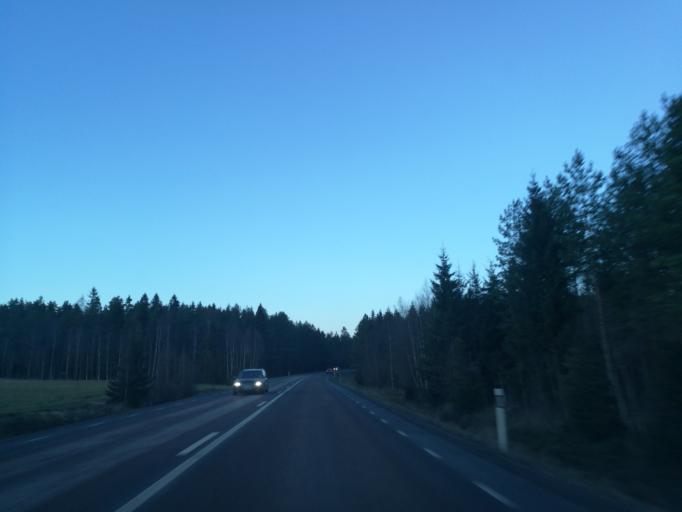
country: SE
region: Vaermland
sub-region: Eda Kommun
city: Charlottenberg
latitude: 59.8957
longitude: 12.2791
